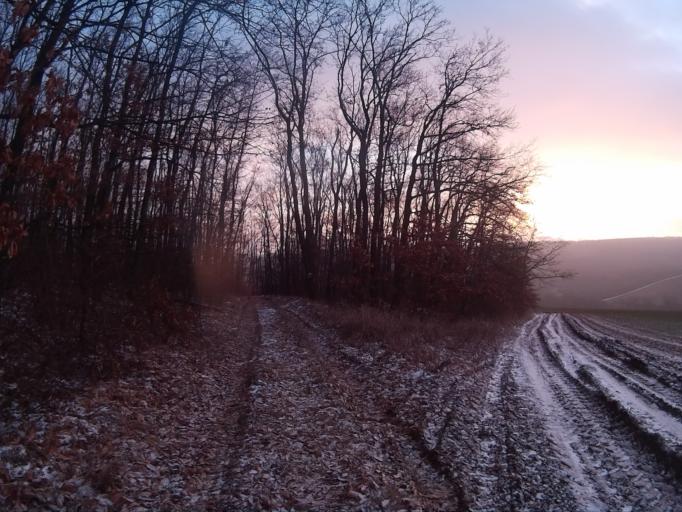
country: HU
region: Borsod-Abauj-Zemplen
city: Szendro
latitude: 48.4134
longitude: 20.8730
